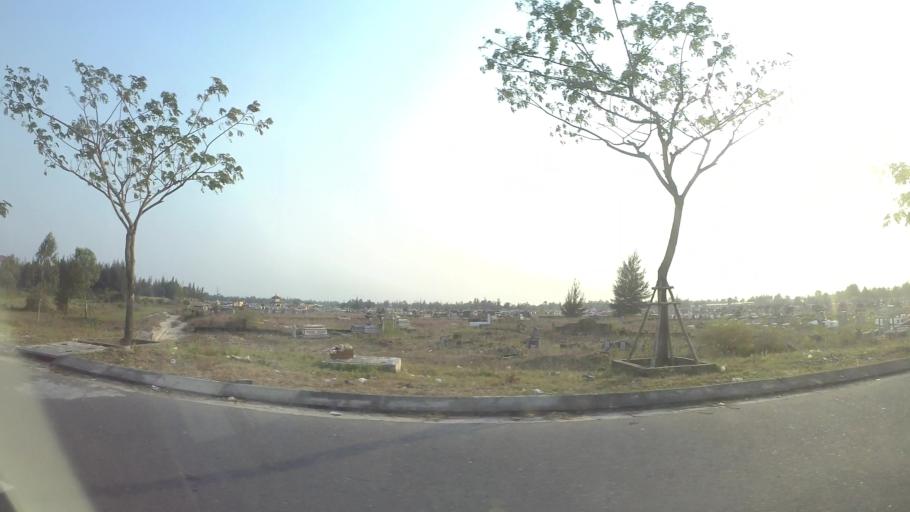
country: VN
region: Da Nang
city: Ngu Hanh Son
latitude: 15.9837
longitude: 108.2432
